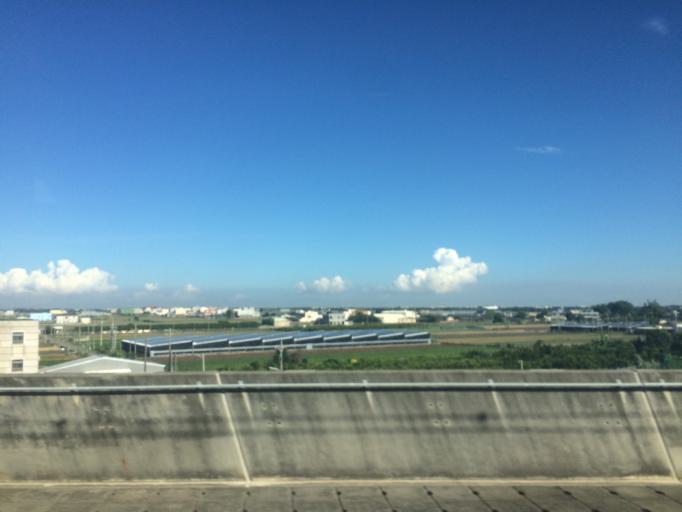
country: TW
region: Taiwan
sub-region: Yunlin
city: Douliu
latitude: 23.6814
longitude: 120.3821
